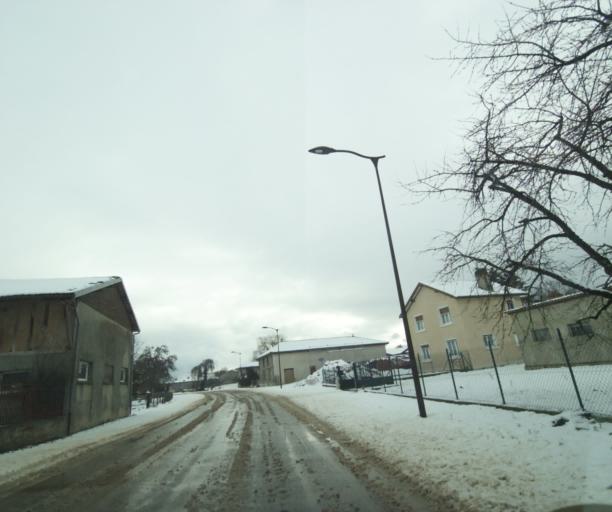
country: FR
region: Champagne-Ardenne
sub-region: Departement de la Haute-Marne
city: Montier-en-Der
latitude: 48.4380
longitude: 4.7126
